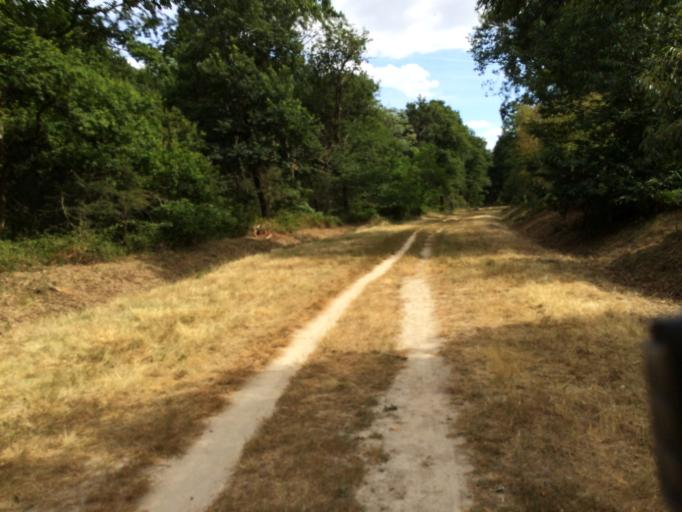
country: FR
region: Ile-de-France
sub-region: Departement de l'Essonne
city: Draveil
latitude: 48.6772
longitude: 2.4425
